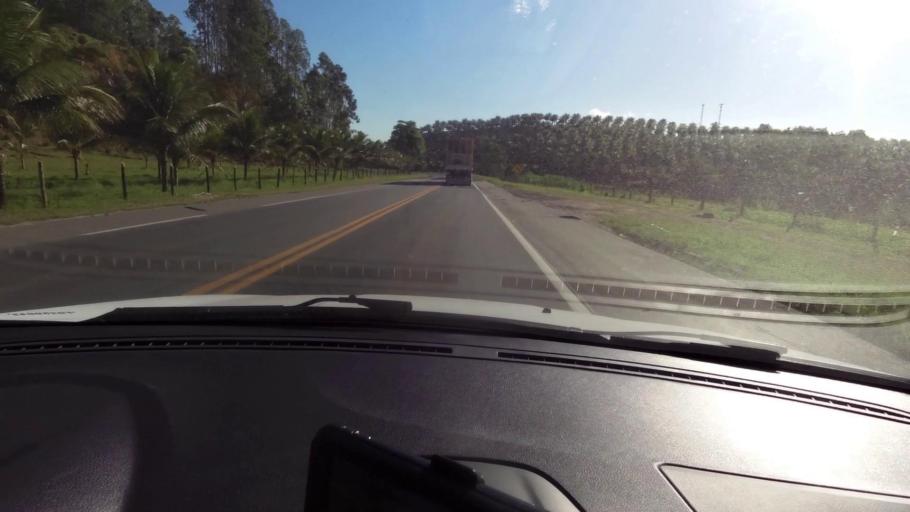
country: BR
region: Espirito Santo
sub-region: Alfredo Chaves
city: Alfredo Chaves
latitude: -20.6845
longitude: -40.6707
